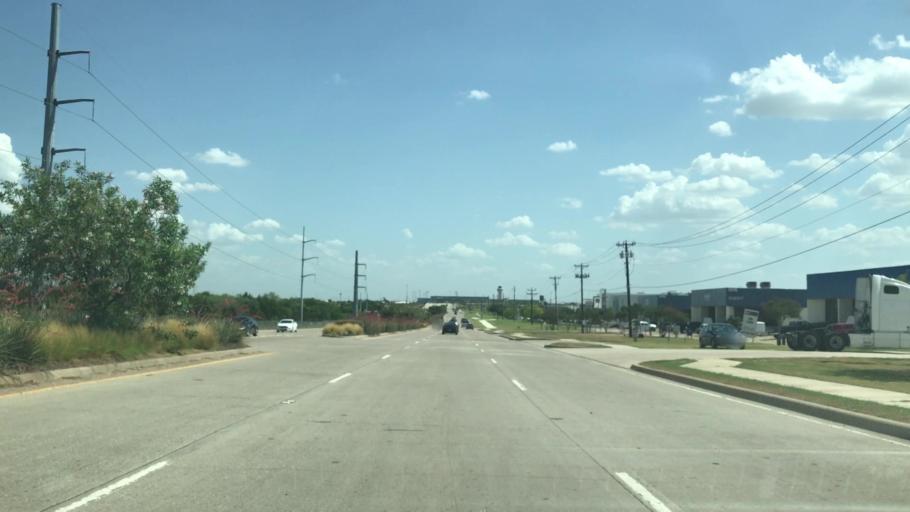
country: US
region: Texas
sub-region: Tarrant County
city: Grapevine
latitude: 32.9315
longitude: -97.0608
